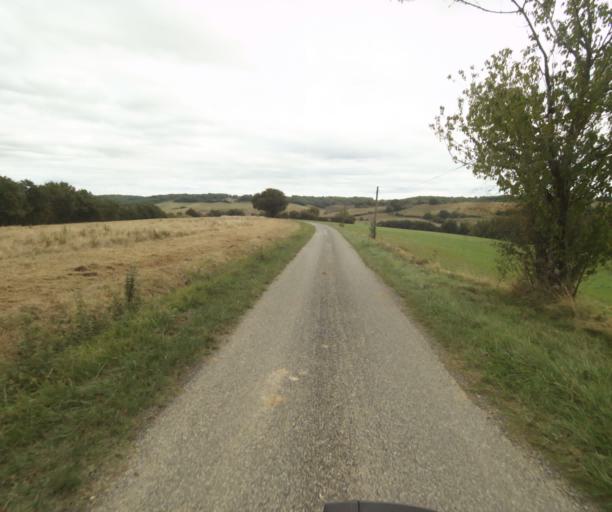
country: FR
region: Midi-Pyrenees
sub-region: Departement du Tarn-et-Garonne
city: Beaumont-de-Lomagne
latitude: 43.8530
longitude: 1.0755
